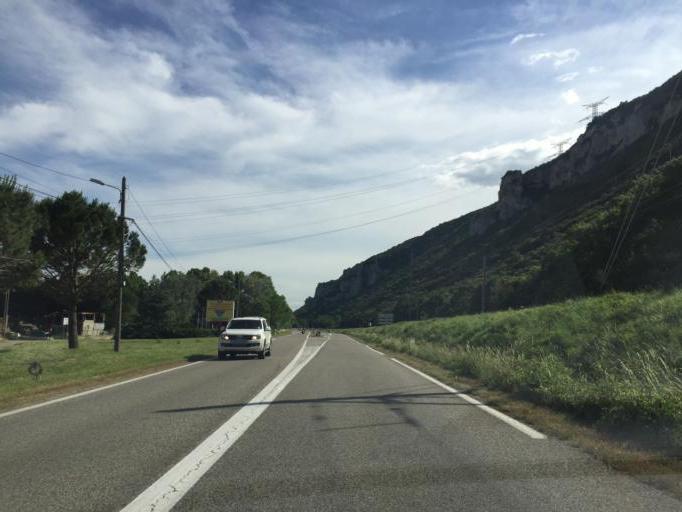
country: FR
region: Rhone-Alpes
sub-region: Departement de l'Ardeche
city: Cruas
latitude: 44.6378
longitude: 4.7477
